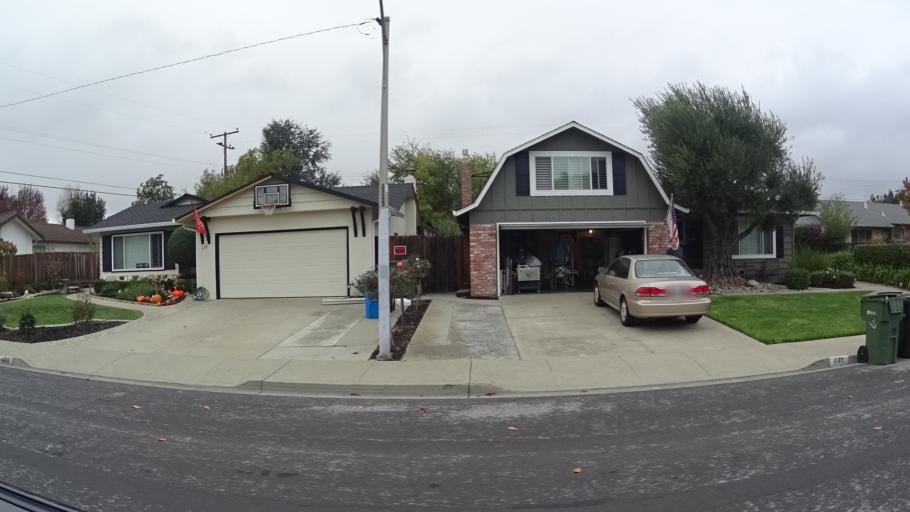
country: US
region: California
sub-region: Santa Clara County
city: Santa Clara
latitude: 37.3335
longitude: -121.9899
